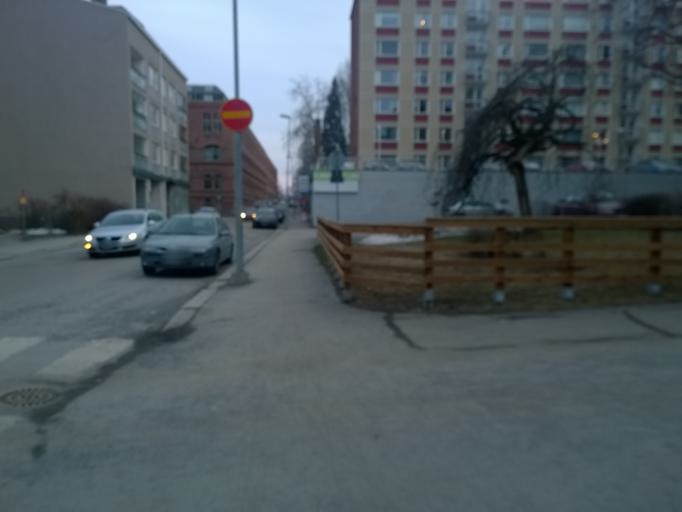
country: FI
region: Pirkanmaa
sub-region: Tampere
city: Tampere
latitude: 61.4933
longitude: 23.7509
